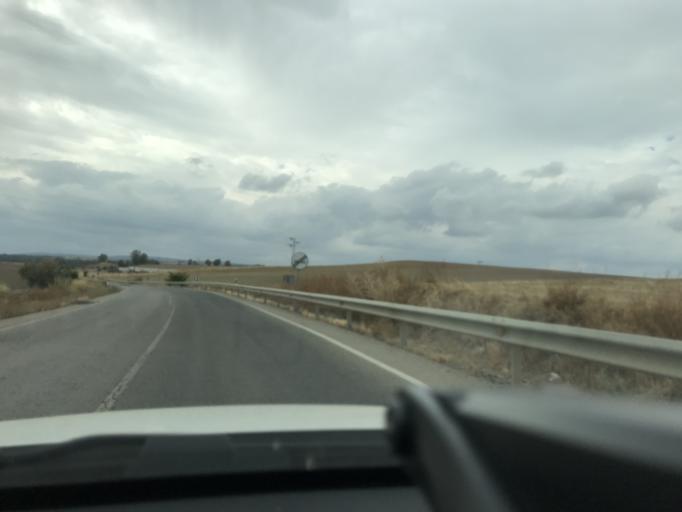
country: ES
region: Andalusia
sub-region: Provincia de Sevilla
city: Villanueva del Rio y Minas
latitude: 37.6353
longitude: -5.7102
